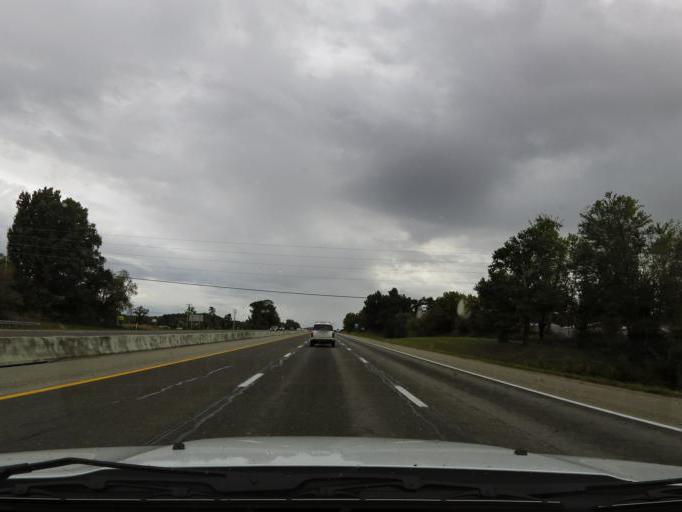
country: US
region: Kentucky
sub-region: Laurel County
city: London
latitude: 37.0775
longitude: -84.0991
